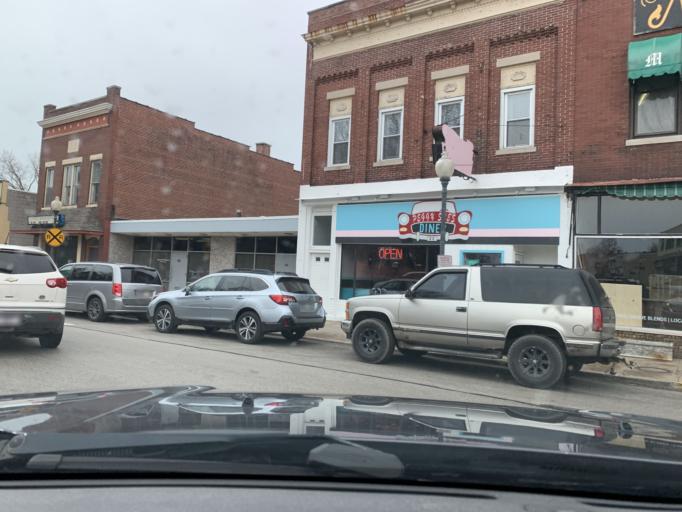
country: US
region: Indiana
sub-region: Porter County
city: Chesterton
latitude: 41.6107
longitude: -87.0523
